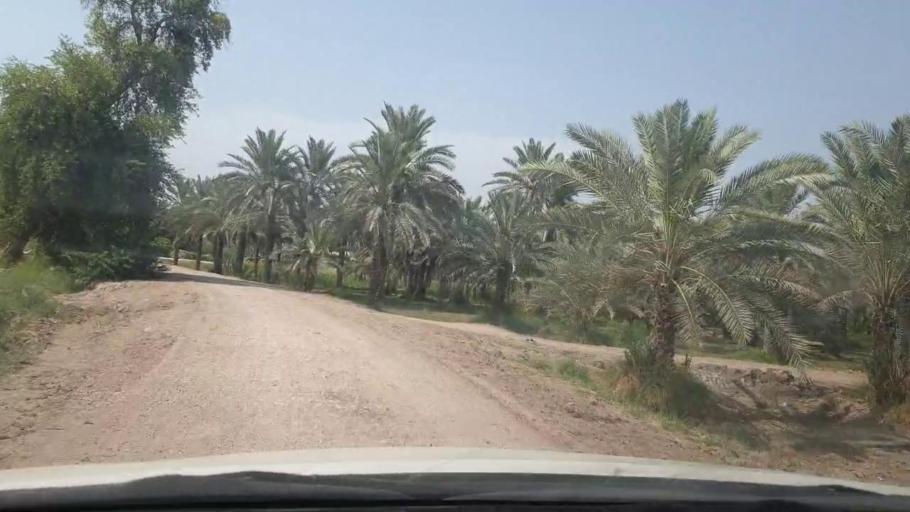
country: PK
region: Sindh
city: Rohri
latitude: 27.5936
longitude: 68.8508
